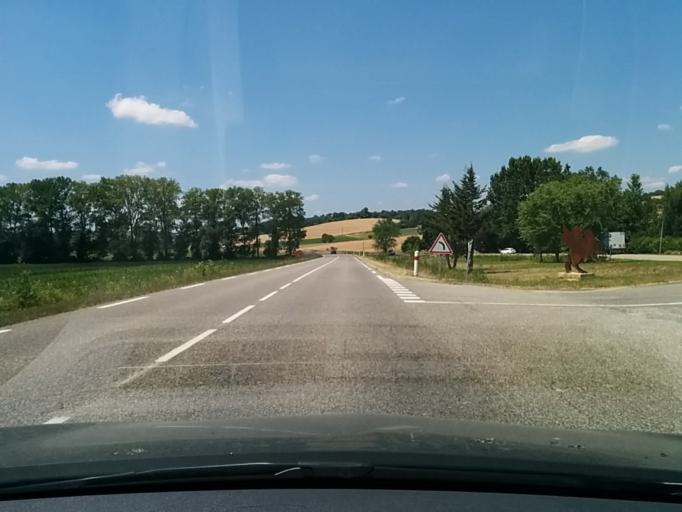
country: FR
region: Midi-Pyrenees
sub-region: Departement du Gers
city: Jegun
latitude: 43.6892
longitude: 0.4796
